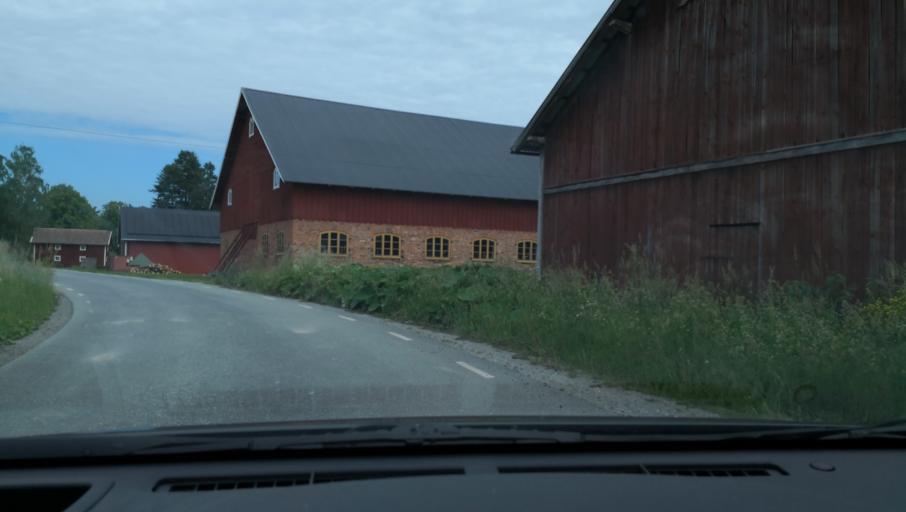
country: SE
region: Uppsala
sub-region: Habo Kommun
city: Balsta
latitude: 59.6947
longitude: 17.4798
